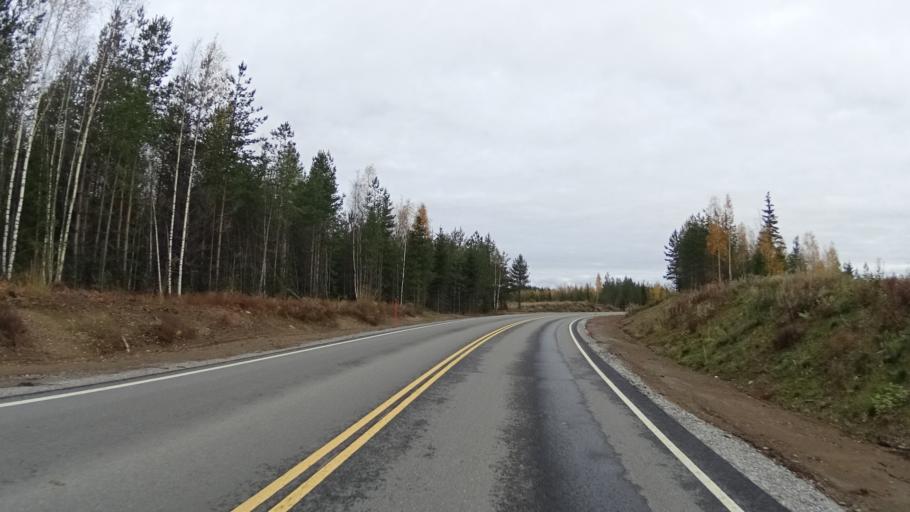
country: FI
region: South Karelia
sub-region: Lappeenranta
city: Lemi
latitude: 60.9950
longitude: 27.9251
